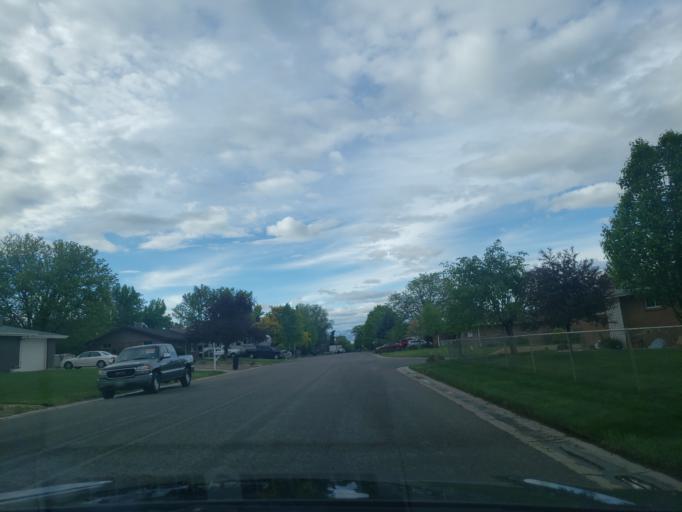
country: US
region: Colorado
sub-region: Mesa County
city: Redlands
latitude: 39.0940
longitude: -108.6588
